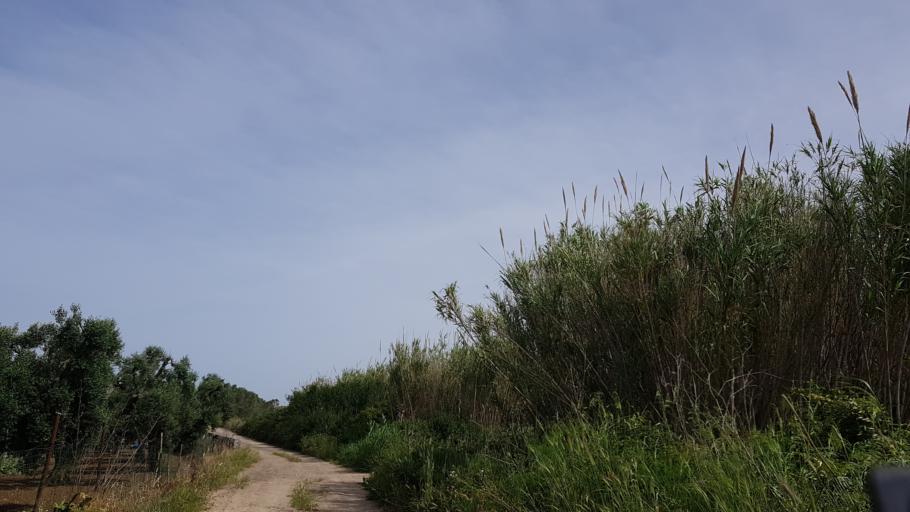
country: IT
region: Apulia
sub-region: Provincia di Brindisi
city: La Rosa
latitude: 40.5903
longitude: 18.0001
